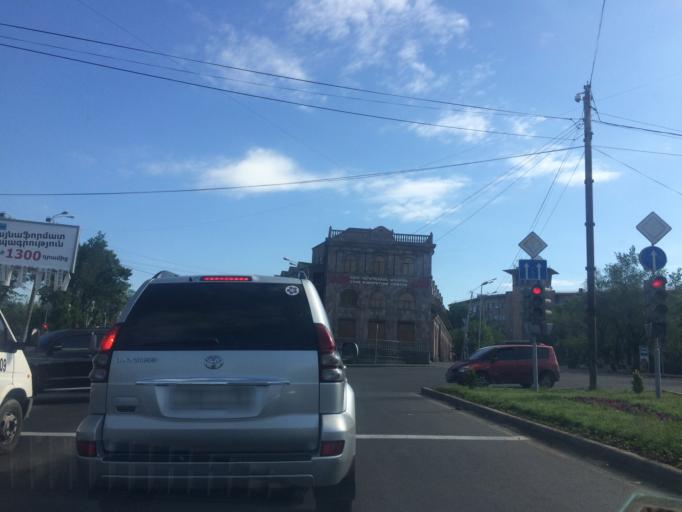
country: AM
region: Yerevan
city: Yerevan
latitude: 40.2094
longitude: 44.5297
